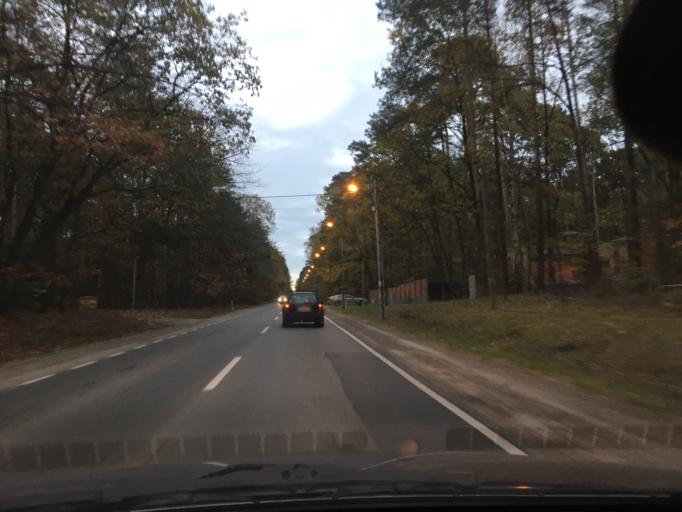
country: PL
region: Masovian Voivodeship
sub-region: Powiat piaseczynski
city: Lesznowola
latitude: 52.1001
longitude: 20.8954
